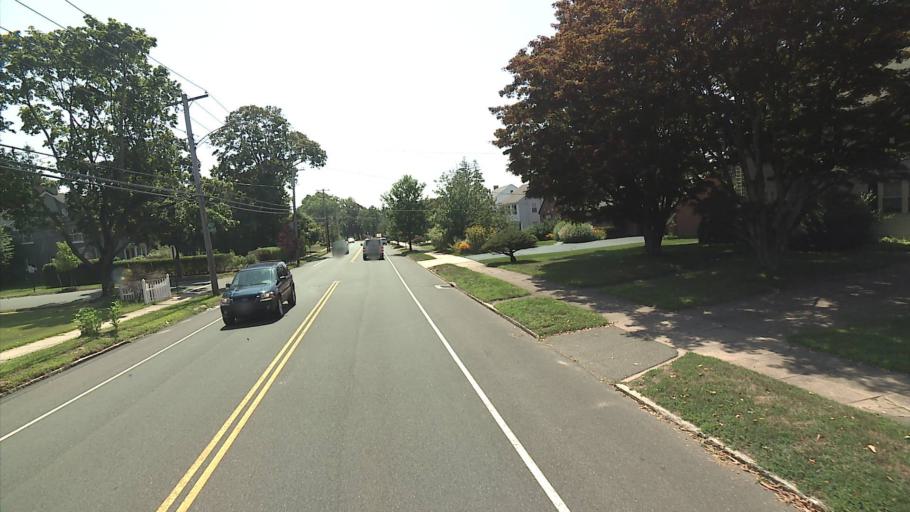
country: US
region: Connecticut
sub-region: New Haven County
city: East Haven
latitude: 41.2738
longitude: -72.8966
